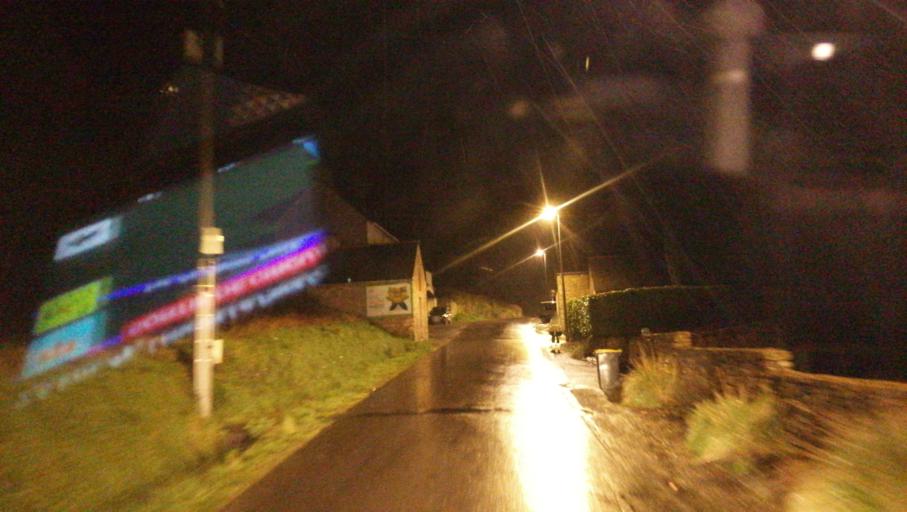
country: FR
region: Brittany
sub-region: Departement des Cotes-d'Armor
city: Le Foeil
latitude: 48.4803
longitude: -2.9615
